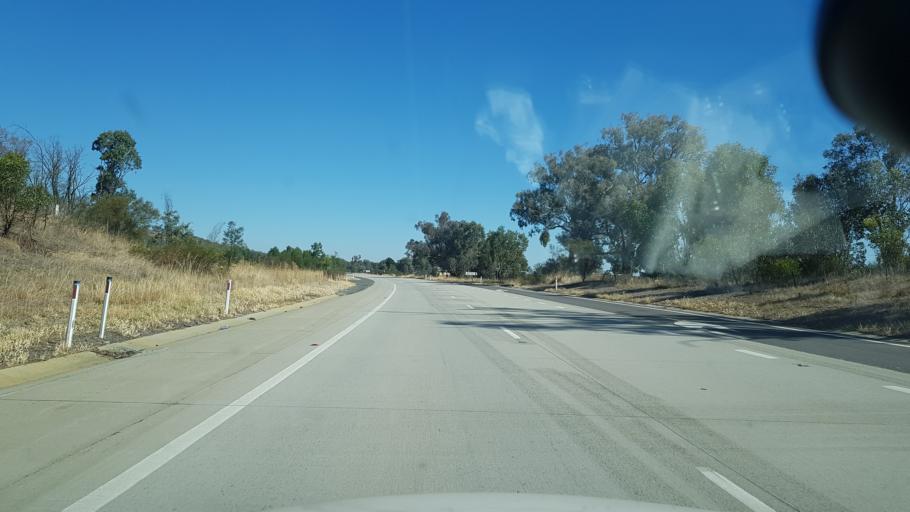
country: AU
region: New South Wales
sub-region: Greater Hume Shire
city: Holbrook
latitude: -35.8955
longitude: 147.1682
